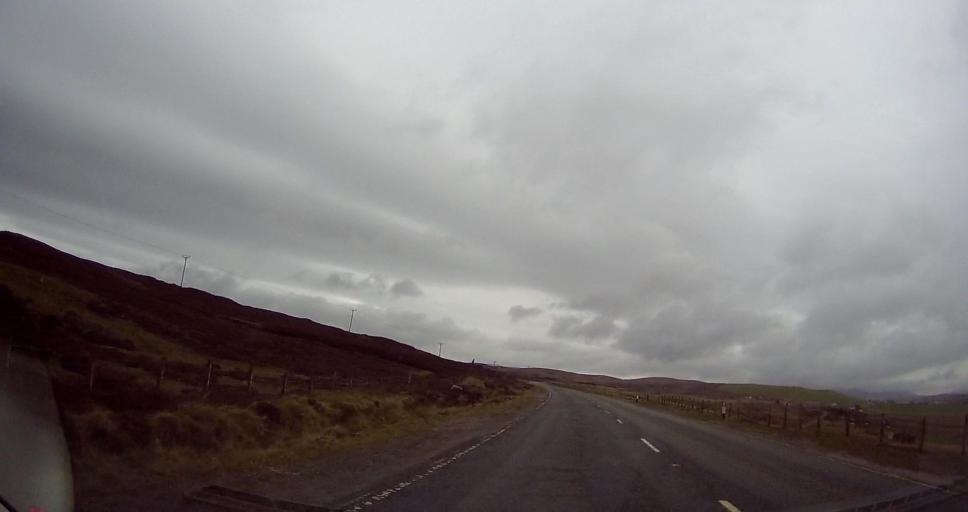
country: GB
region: Scotland
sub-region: Shetland Islands
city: Lerwick
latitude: 60.2256
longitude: -1.2352
